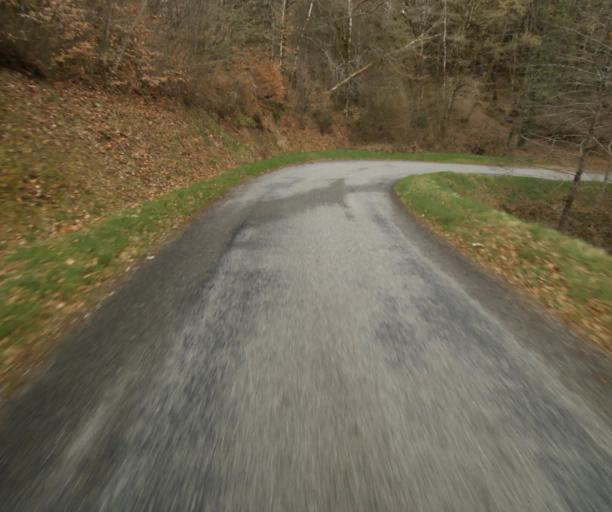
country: FR
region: Limousin
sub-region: Departement de la Correze
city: Argentat
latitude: 45.2284
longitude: 1.9850
